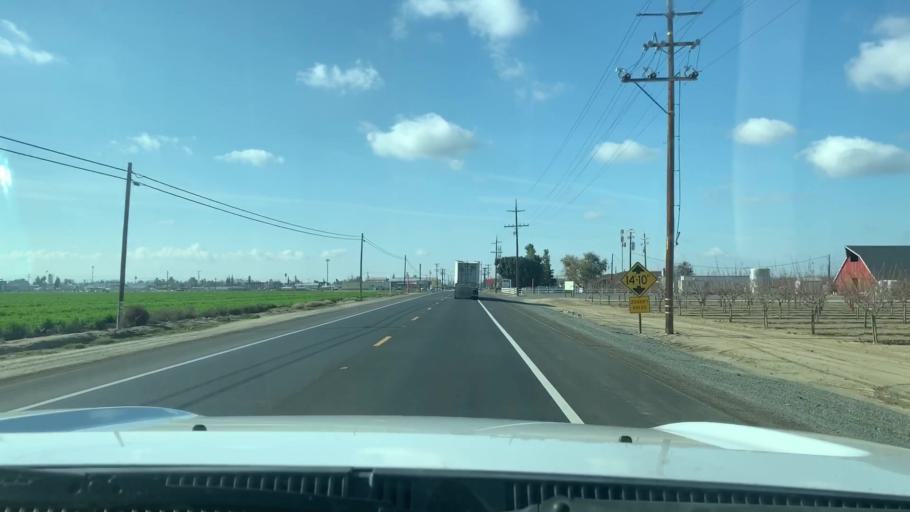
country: US
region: California
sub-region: Kern County
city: Wasco
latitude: 35.6016
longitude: -119.3224
